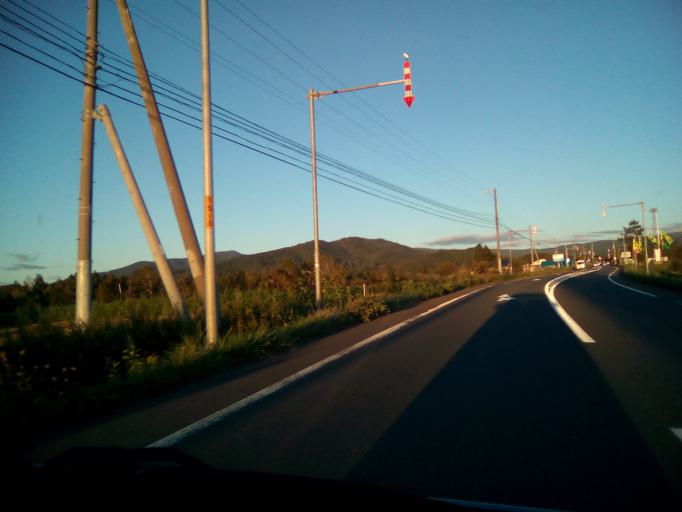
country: JP
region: Hokkaido
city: Niseko Town
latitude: 42.6650
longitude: 140.8215
